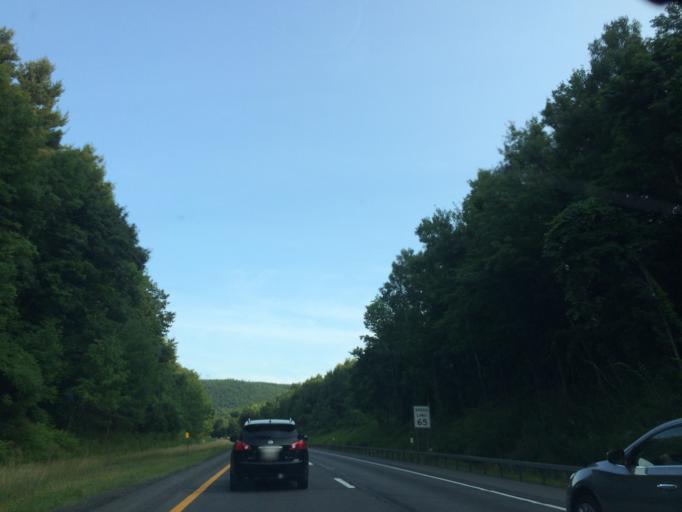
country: US
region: Massachusetts
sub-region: Berkshire County
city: Richmond
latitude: 42.3756
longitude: -73.4627
